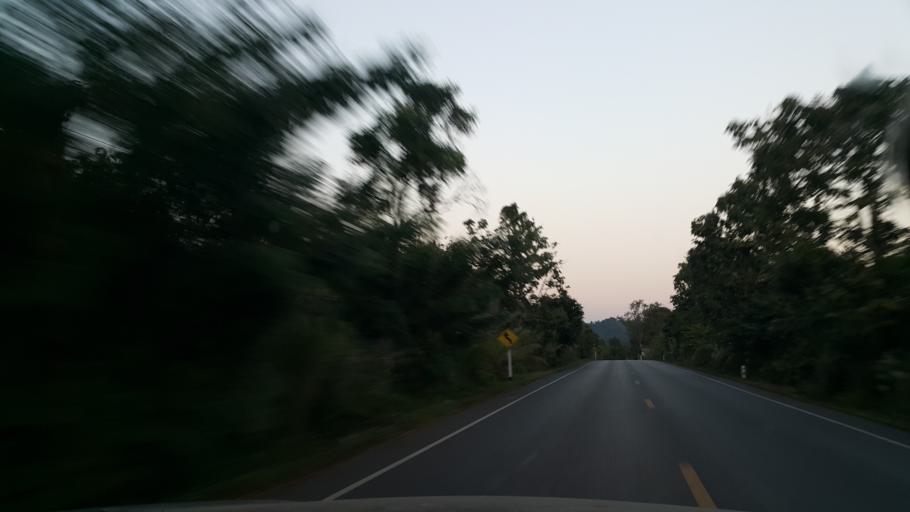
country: TH
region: Phrae
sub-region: Amphoe Wang Chin
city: Wang Chin
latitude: 17.9656
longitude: 99.6131
